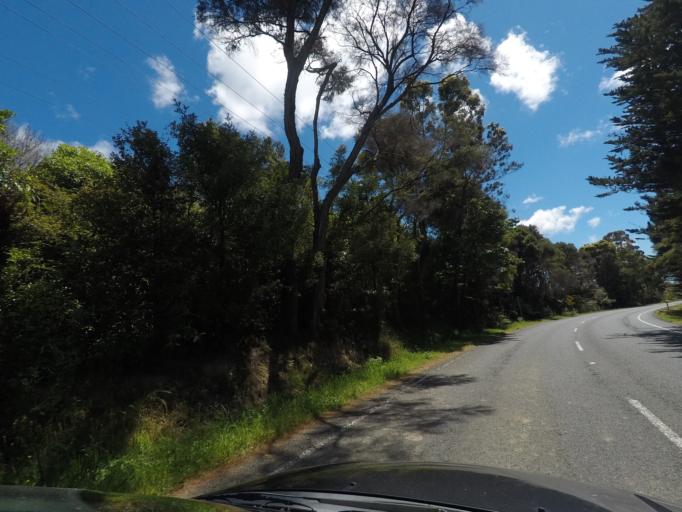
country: NZ
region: Auckland
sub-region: Auckland
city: Rothesay Bay
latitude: -36.7385
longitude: 174.6751
